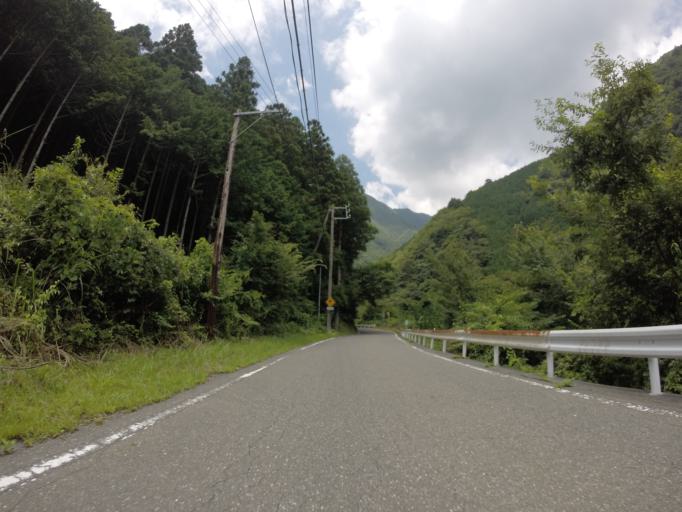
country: JP
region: Shizuoka
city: Fujinomiya
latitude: 35.2884
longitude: 138.3399
